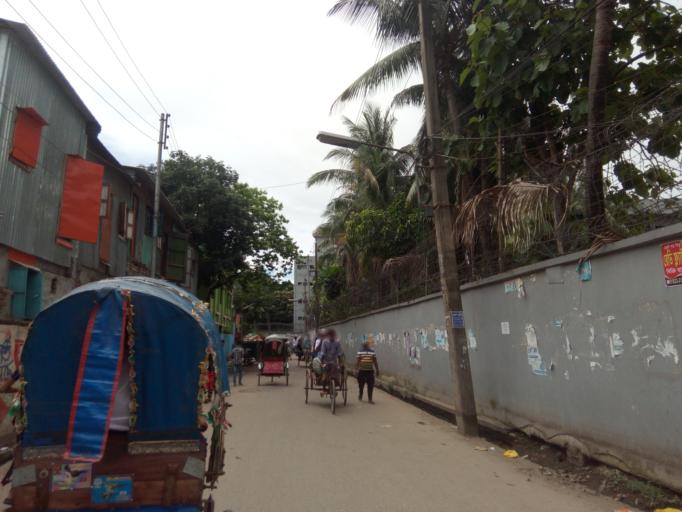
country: BD
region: Dhaka
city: Azimpur
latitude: 23.7290
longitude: 90.3757
